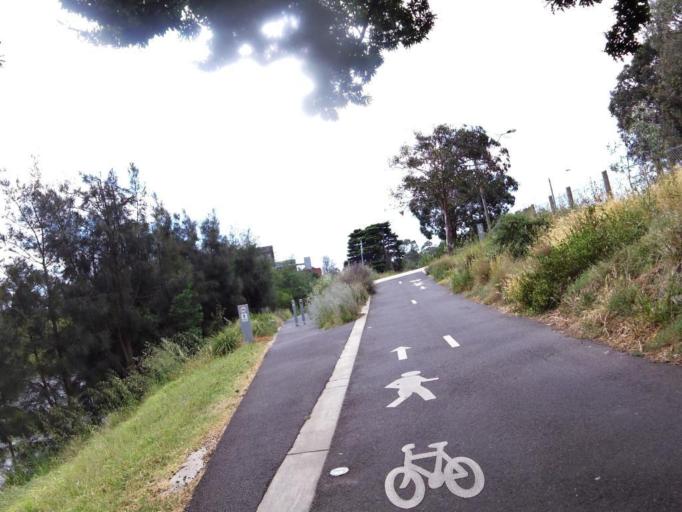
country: AU
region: Victoria
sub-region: Stonnington
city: Toorak
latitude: -37.8324
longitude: 145.0109
